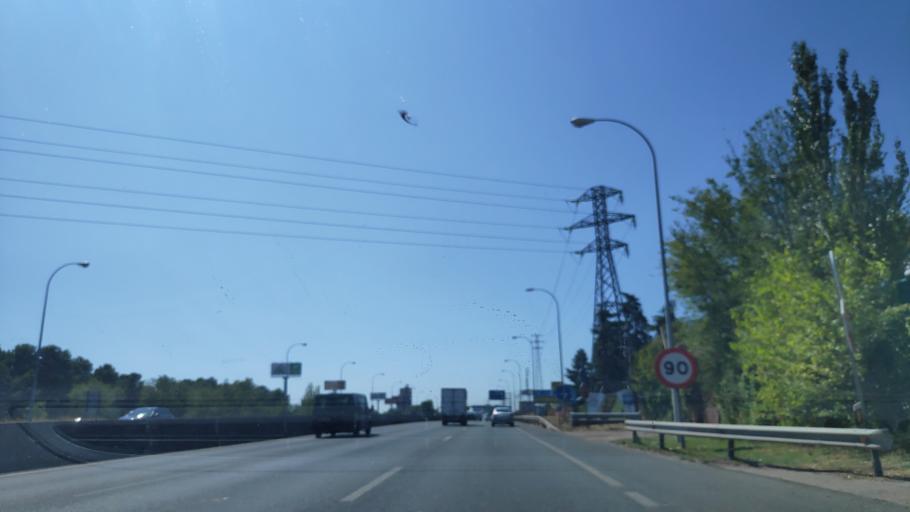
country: ES
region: Madrid
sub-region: Provincia de Madrid
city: Villaverde
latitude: 40.3482
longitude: -3.7231
